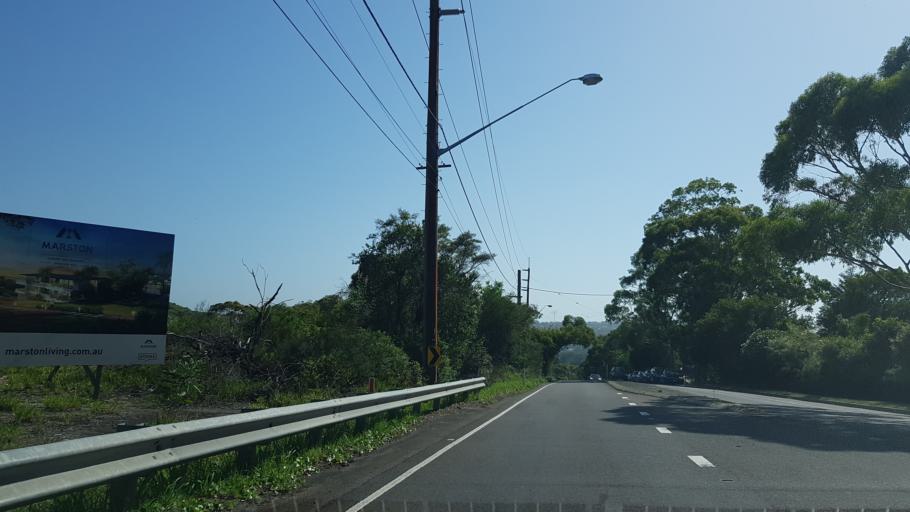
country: AU
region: New South Wales
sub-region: Warringah
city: Narraweena
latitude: -33.7444
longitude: 151.2653
